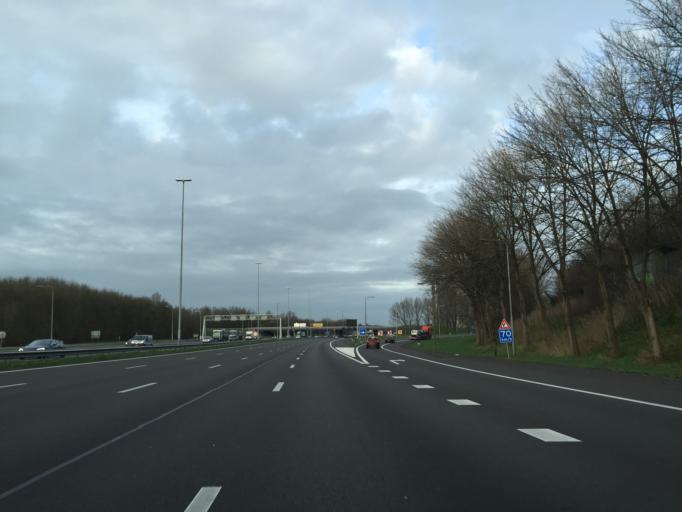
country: NL
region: Utrecht
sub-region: Gemeente Nieuwegein
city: Nieuwegein
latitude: 52.0219
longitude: 5.0653
